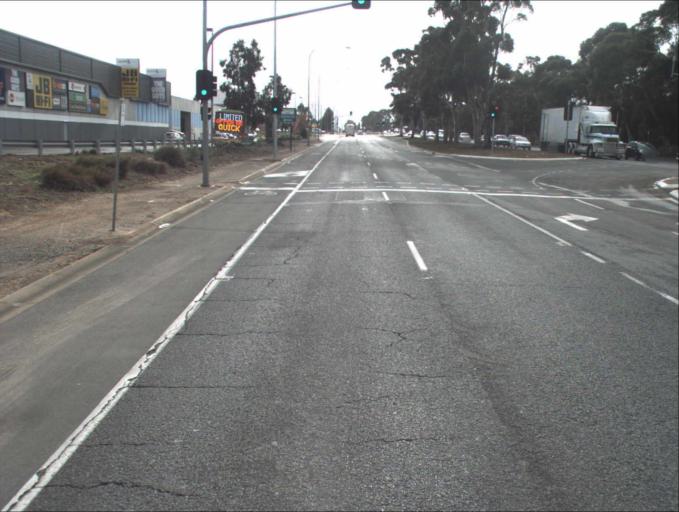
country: AU
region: South Australia
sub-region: Port Adelaide Enfield
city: Enfield
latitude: -34.8397
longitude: 138.6063
